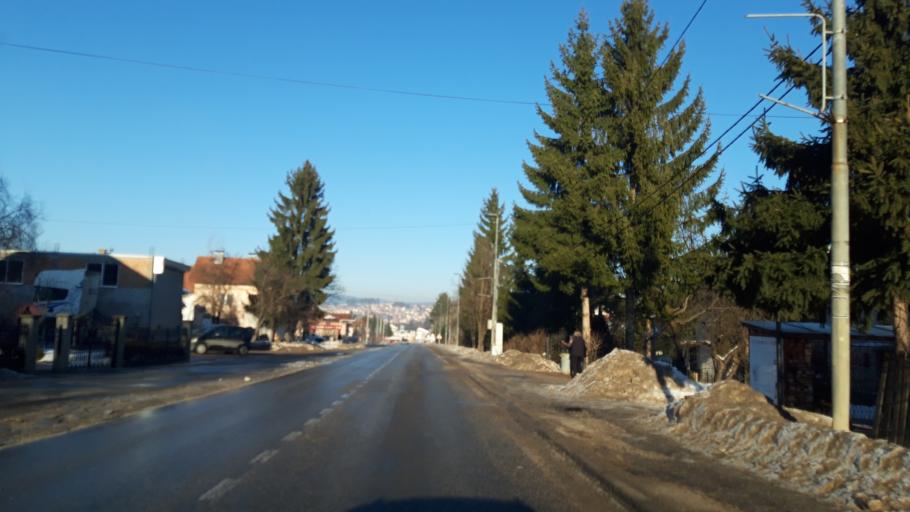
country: BA
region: Republika Srpska
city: Sokolac
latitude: 43.9298
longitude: 18.7885
